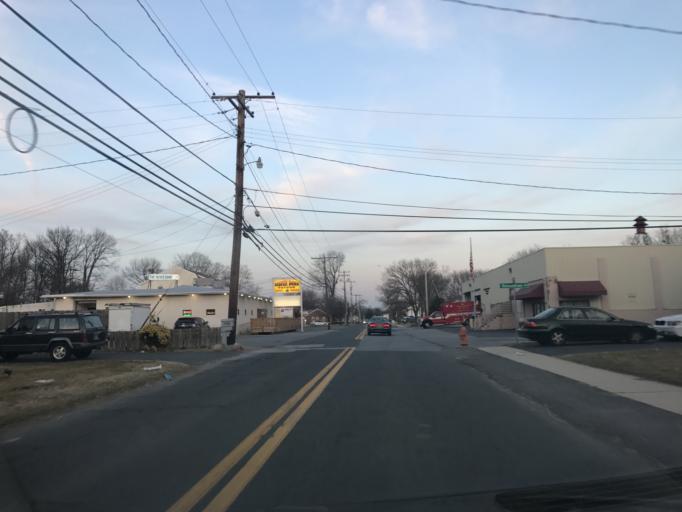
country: US
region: Maryland
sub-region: Baltimore County
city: Middle River
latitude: 39.3073
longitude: -76.4321
